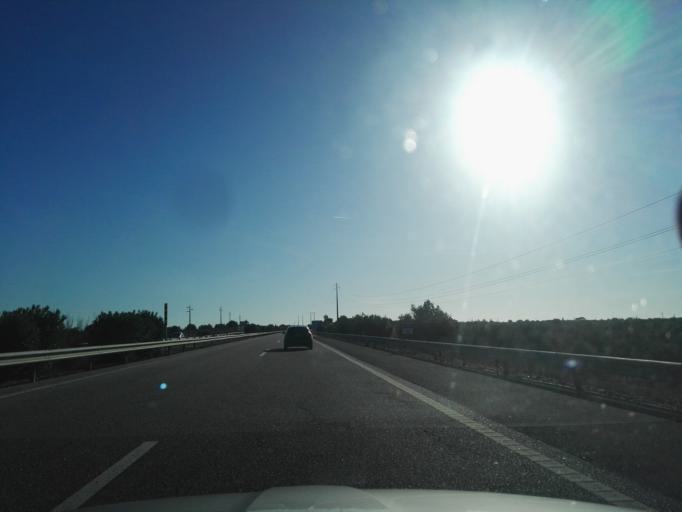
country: PT
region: Santarem
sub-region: Alcanena
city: Alcanena
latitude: 39.4794
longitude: -8.6164
